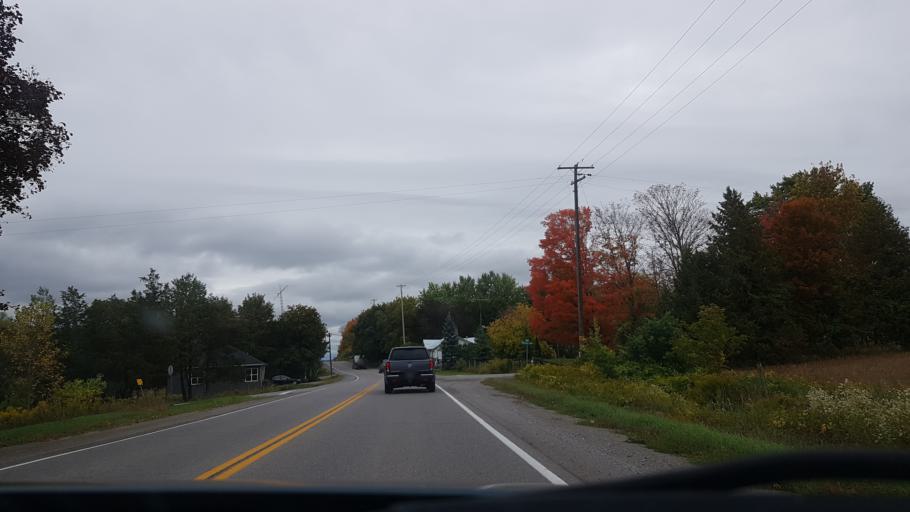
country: CA
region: Ontario
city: Omemee
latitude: 44.2246
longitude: -78.4795
